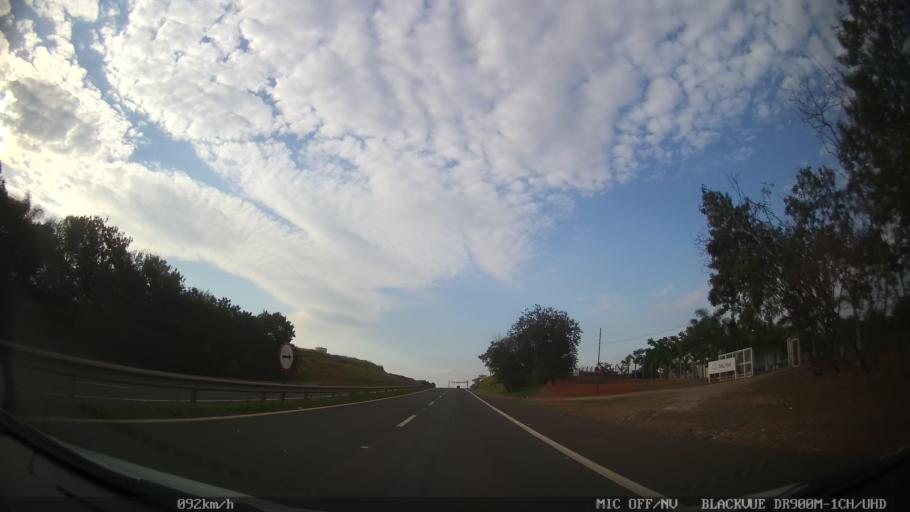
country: BR
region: Sao Paulo
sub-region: Cosmopolis
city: Cosmopolis
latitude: -22.6239
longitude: -47.2012
